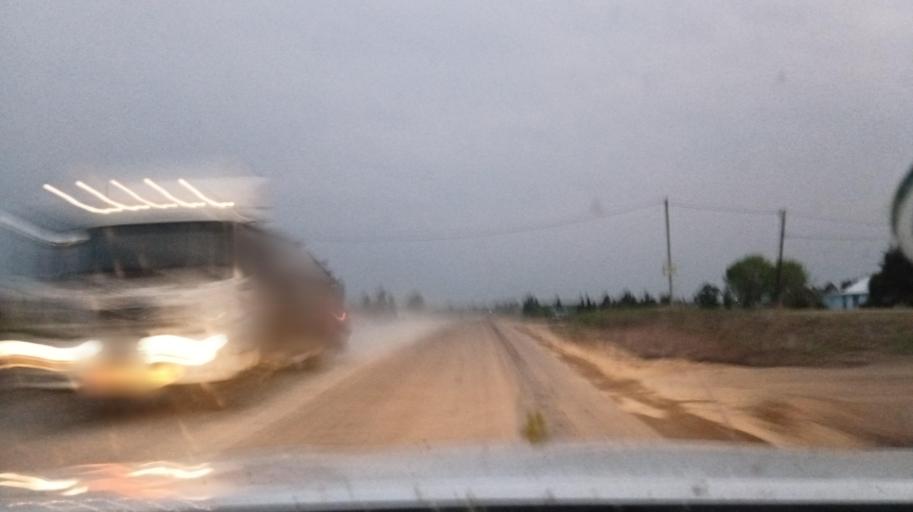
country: UY
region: Canelones
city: Santa Rosa
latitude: -34.5632
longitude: -56.1022
